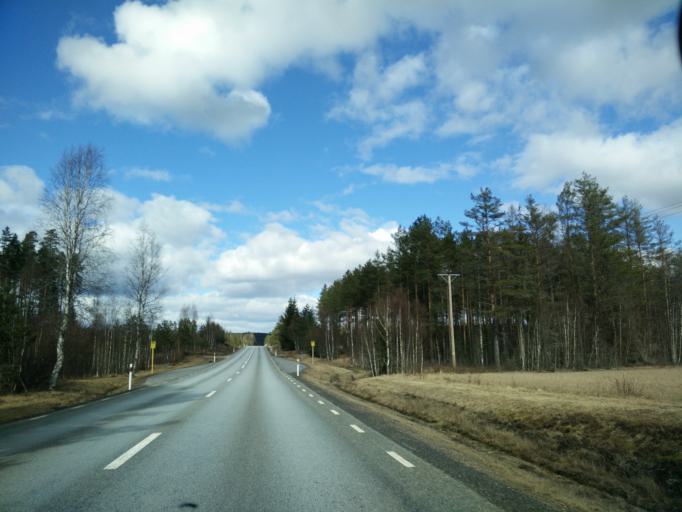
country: SE
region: Vaermland
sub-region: Munkfors Kommun
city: Munkfors
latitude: 59.9323
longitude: 13.5770
